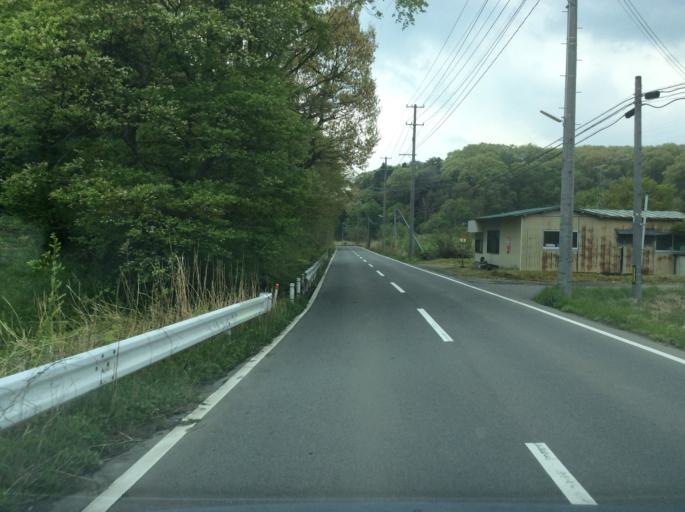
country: JP
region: Fukushima
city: Koriyama
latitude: 37.3901
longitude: 140.4285
